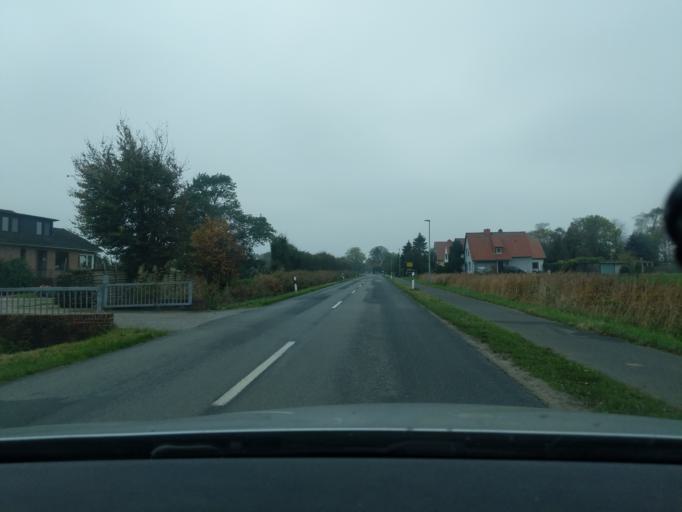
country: DE
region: Lower Saxony
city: Otterndorf
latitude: 53.8229
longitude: 8.8546
